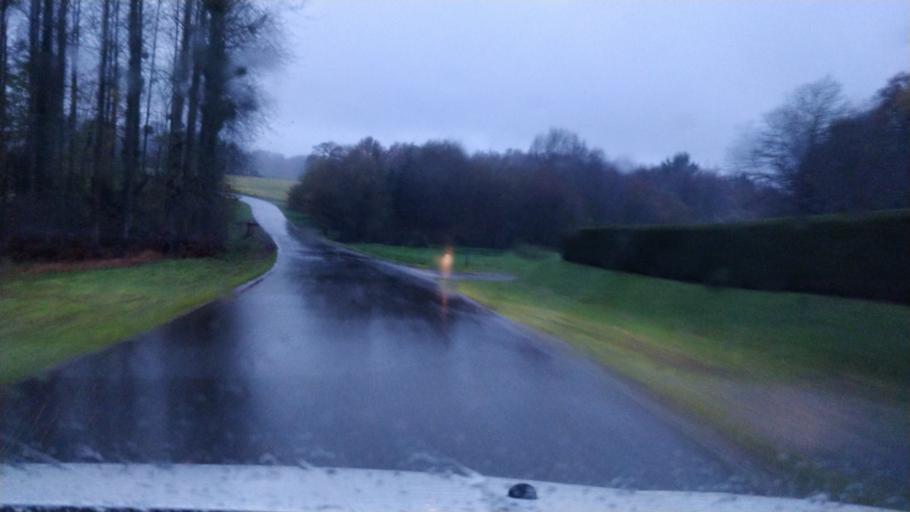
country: FR
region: Brittany
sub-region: Departement du Morbihan
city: Meneac
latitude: 48.1979
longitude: -2.5103
